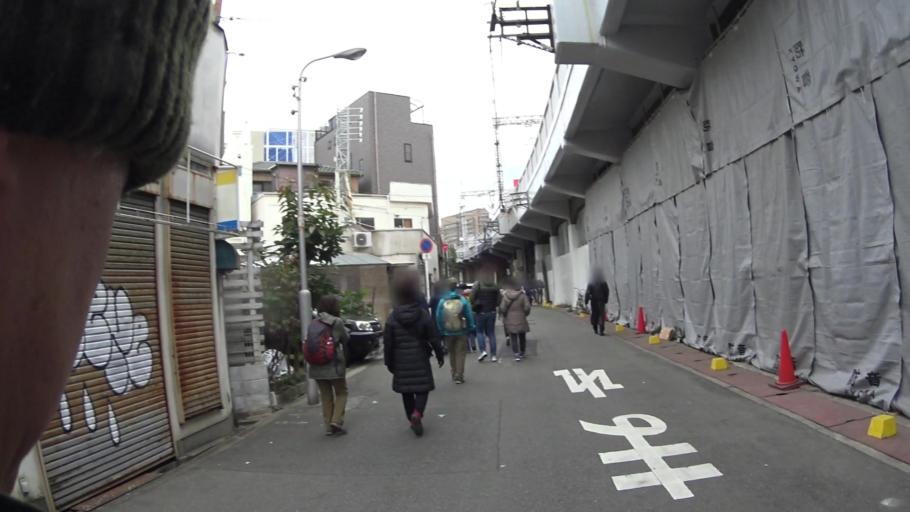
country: JP
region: Osaka
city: Osaka-shi
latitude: 34.7107
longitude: 135.4902
